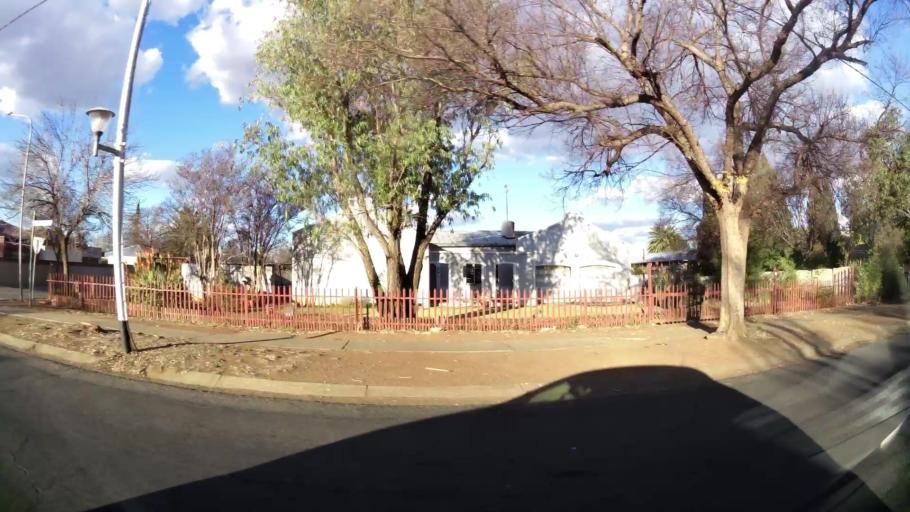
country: ZA
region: North-West
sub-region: Dr Kenneth Kaunda District Municipality
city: Potchefstroom
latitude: -26.7296
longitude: 27.0896
